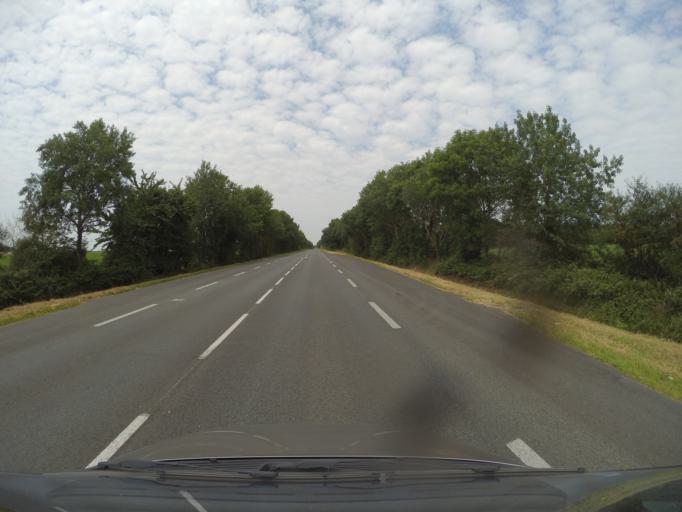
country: FR
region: Pays de la Loire
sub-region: Departement de la Vendee
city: Saint-Georges-de-Montaigu
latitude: 46.9353
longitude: -1.3195
